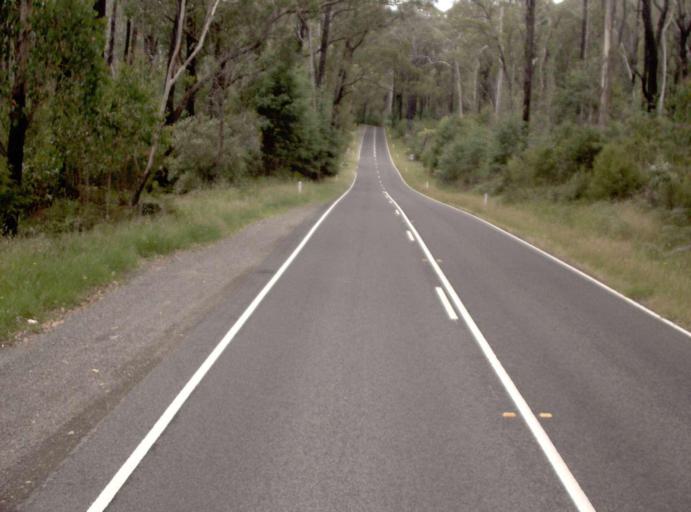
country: AU
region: Victoria
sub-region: Yarra Ranges
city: Healesville
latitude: -37.6295
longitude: 145.5945
